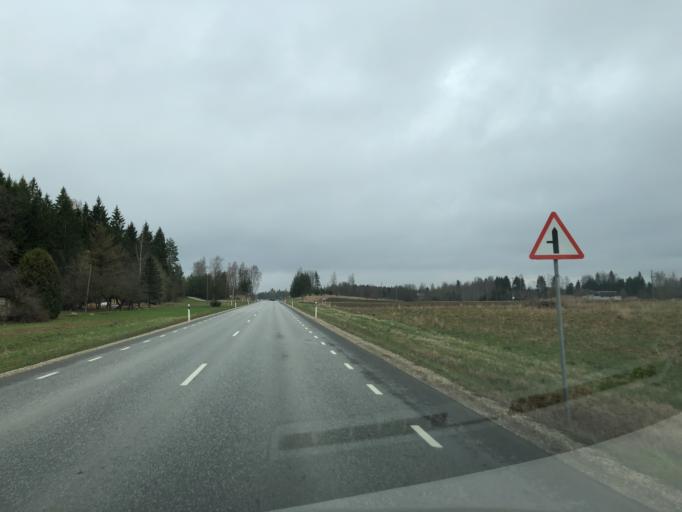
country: EE
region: Jogevamaa
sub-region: Jogeva linn
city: Jogeva
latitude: 58.7673
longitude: 26.3302
